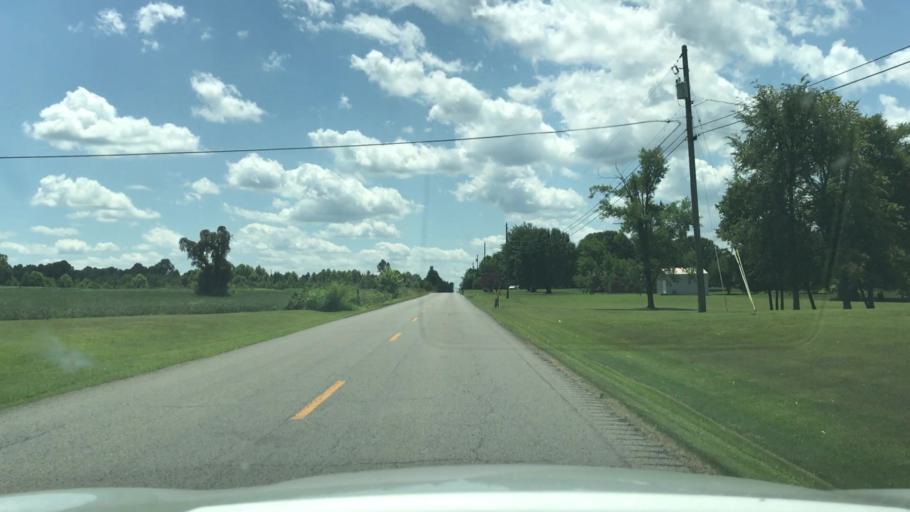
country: US
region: Kentucky
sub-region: Muhlenberg County
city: Greenville
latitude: 37.1712
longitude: -87.2439
